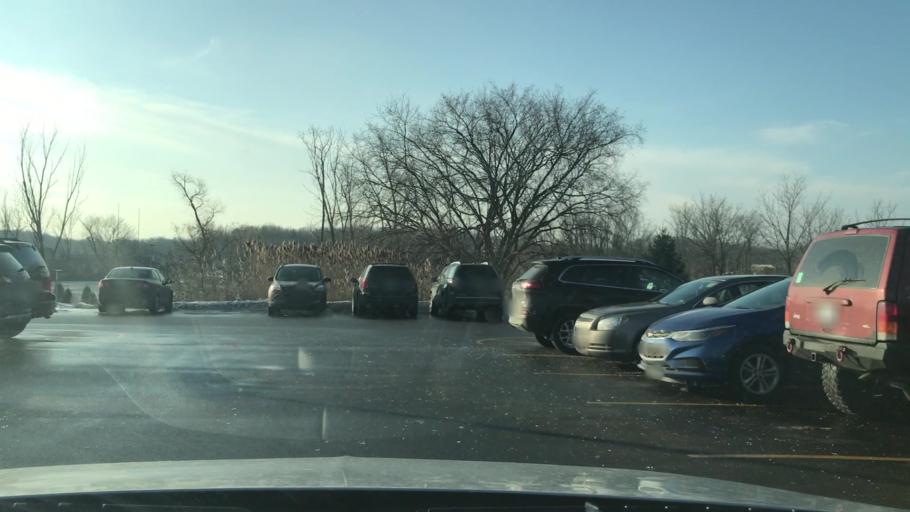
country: US
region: Michigan
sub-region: Oakland County
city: Auburn Hills
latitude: 42.6701
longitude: -83.2174
